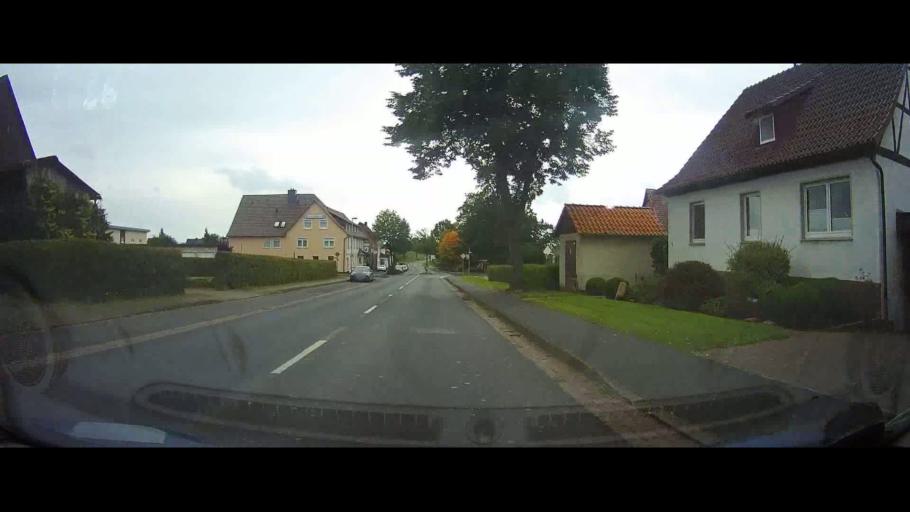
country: DE
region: Lower Saxony
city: Uslar
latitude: 51.6802
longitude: 9.6406
